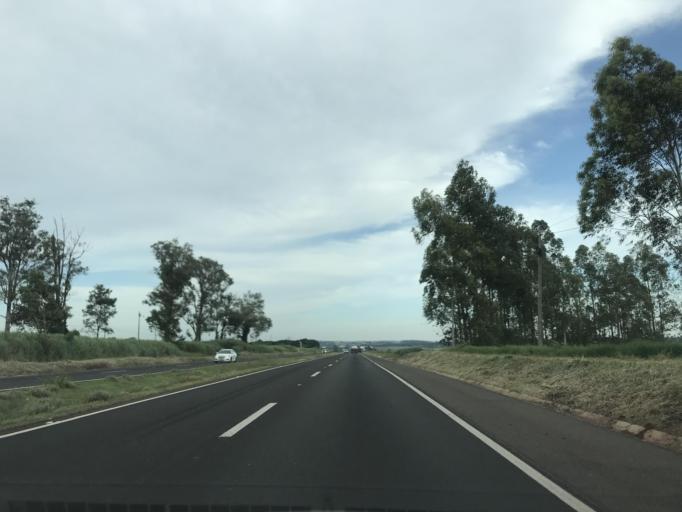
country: BR
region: Parana
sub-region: Alto Parana
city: Alto Parana
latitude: -23.1513
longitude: -52.2720
